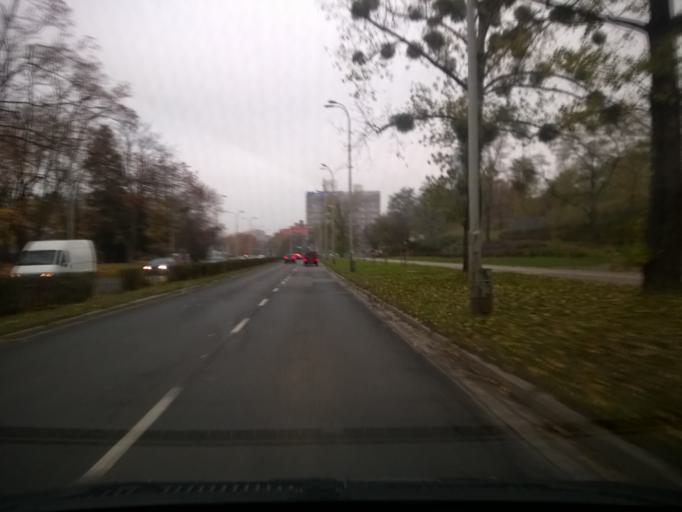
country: PL
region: Lower Silesian Voivodeship
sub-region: Powiat wroclawski
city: Wroclaw
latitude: 51.0892
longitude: 17.0314
